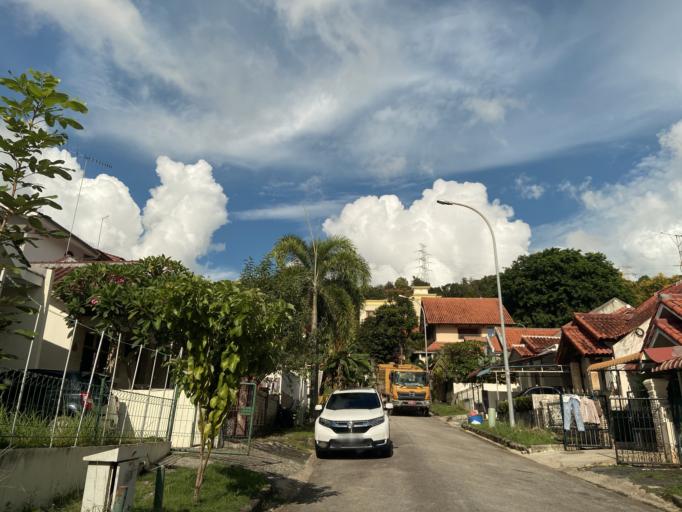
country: SG
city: Singapore
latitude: 1.1125
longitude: 104.0215
